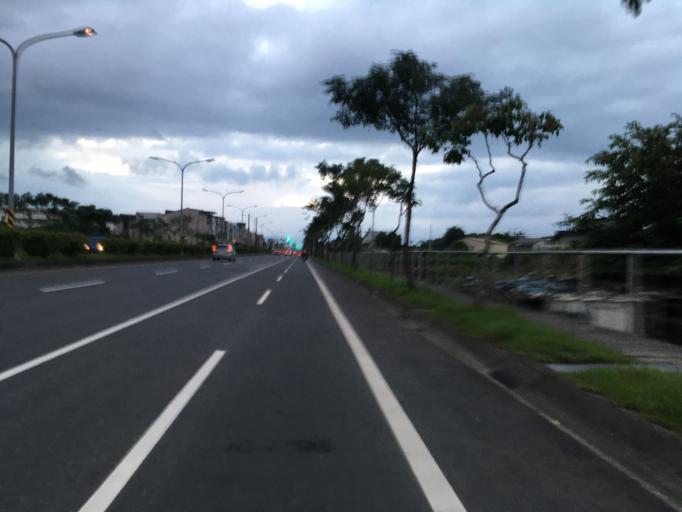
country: TW
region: Taiwan
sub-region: Yilan
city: Yilan
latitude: 24.6201
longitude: 121.8427
